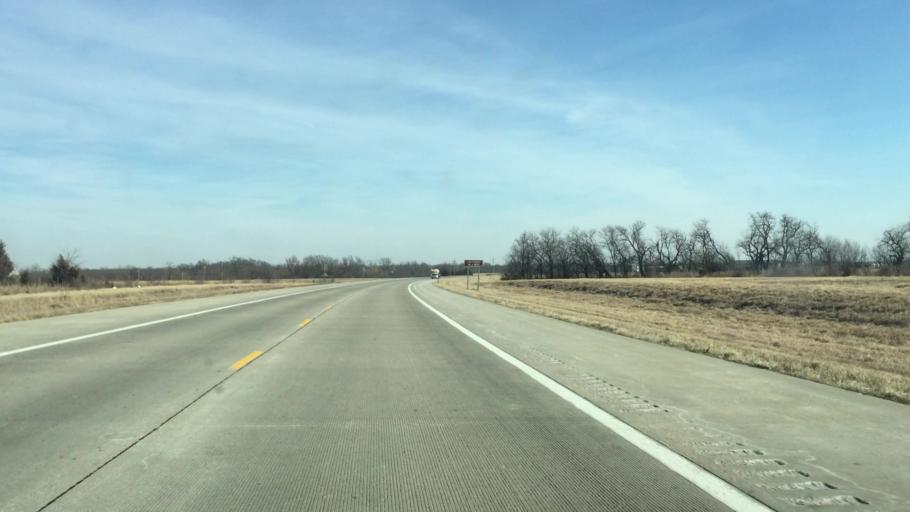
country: US
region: Kansas
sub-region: Labette County
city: Parsons
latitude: 37.3667
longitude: -95.2967
